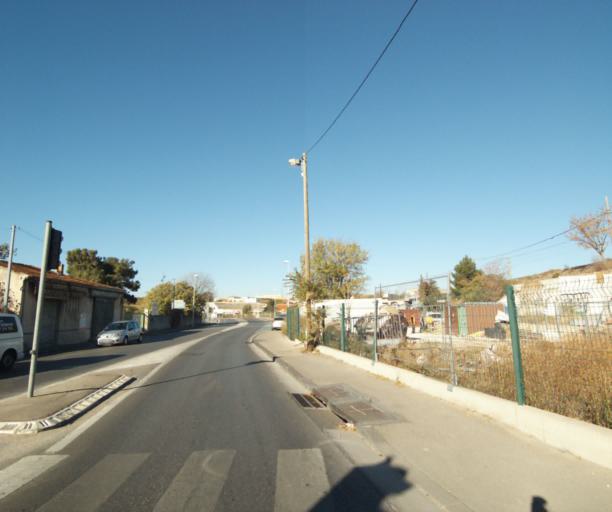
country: FR
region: Provence-Alpes-Cote d'Azur
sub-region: Departement des Bouches-du-Rhone
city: Marseille 12
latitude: 43.2902
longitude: 5.4258
